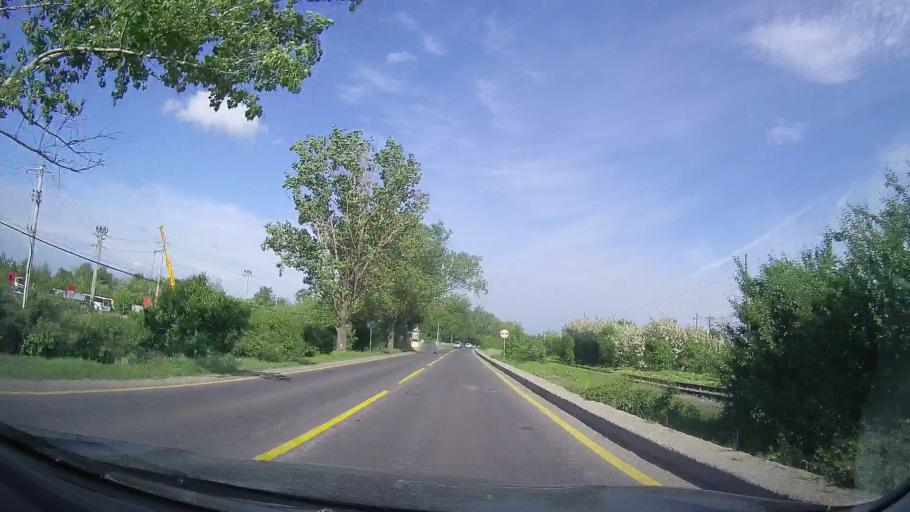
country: RO
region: Ilfov
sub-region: Comuna Magurele
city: Magurele
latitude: 44.3623
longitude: 26.0270
